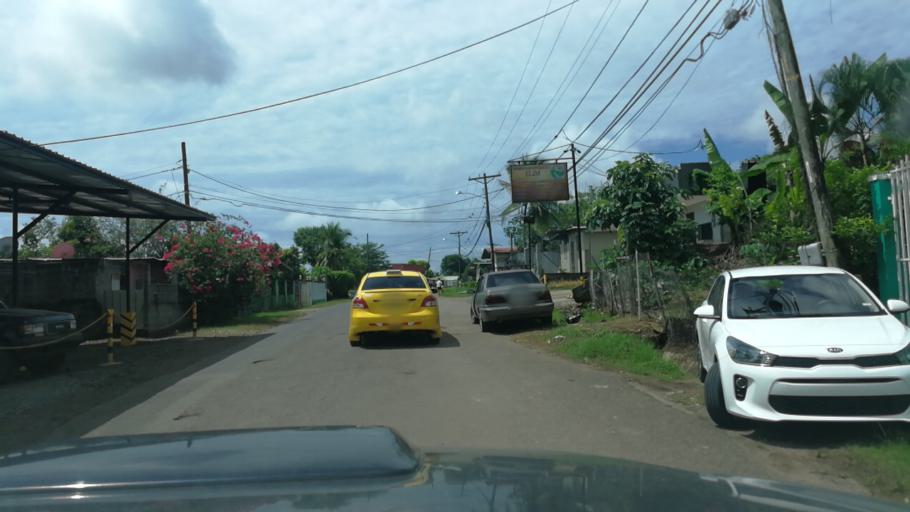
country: PA
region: Panama
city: Tocumen
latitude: 9.1027
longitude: -79.4118
